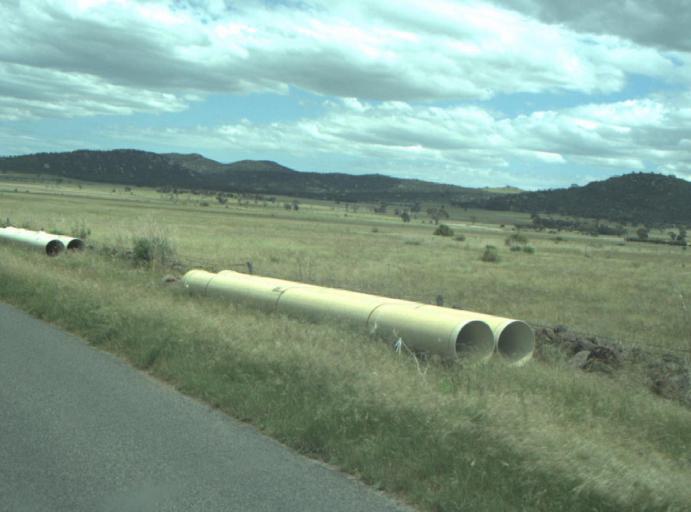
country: AU
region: Victoria
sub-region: Wyndham
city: Little River
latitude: -37.9041
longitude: 144.4639
